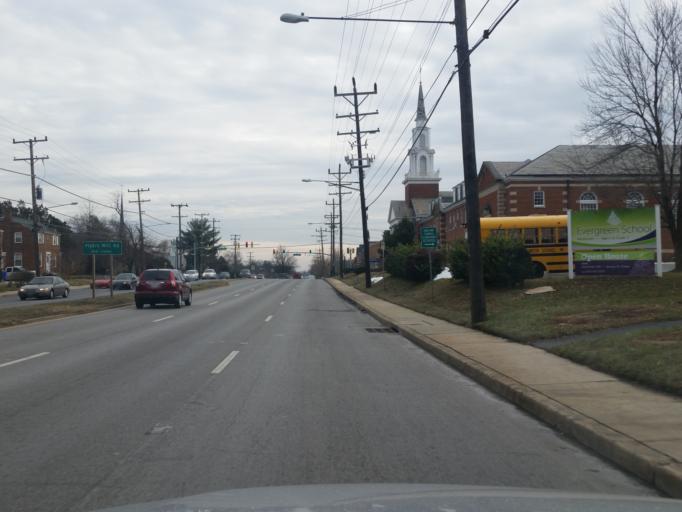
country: US
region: Maryland
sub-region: Montgomery County
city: Wheaton
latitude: 39.0313
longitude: -77.0483
